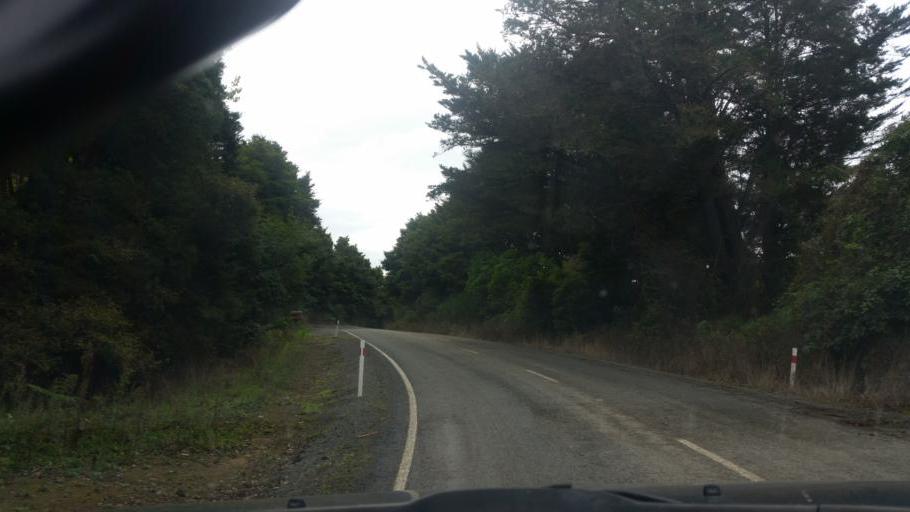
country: NZ
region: Northland
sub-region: Kaipara District
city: Dargaville
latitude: -35.7493
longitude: 173.9051
